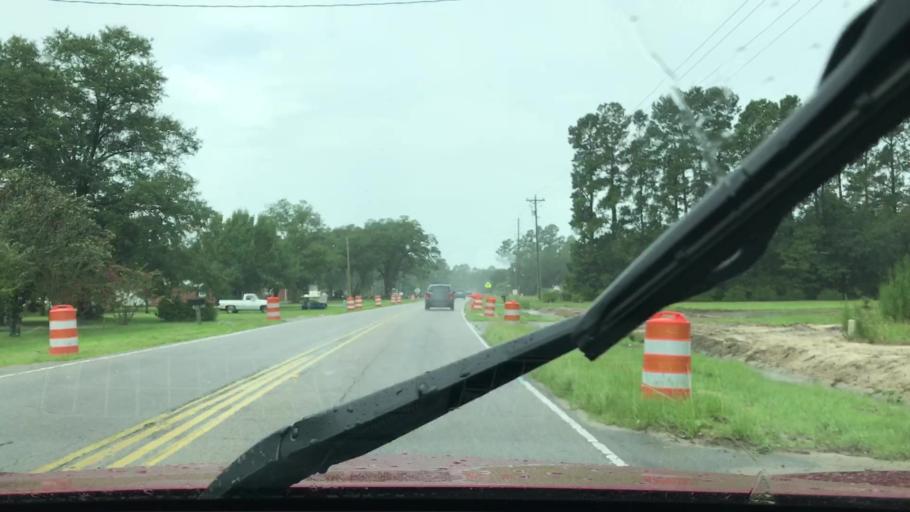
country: US
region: South Carolina
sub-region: Horry County
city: Red Hill
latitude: 33.8752
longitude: -78.9750
